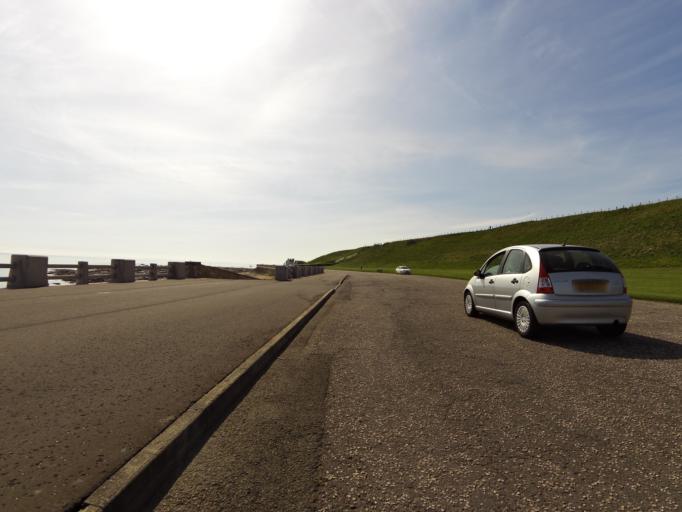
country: GB
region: Scotland
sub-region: Angus
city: Arbroath
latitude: 56.5600
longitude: -2.5702
